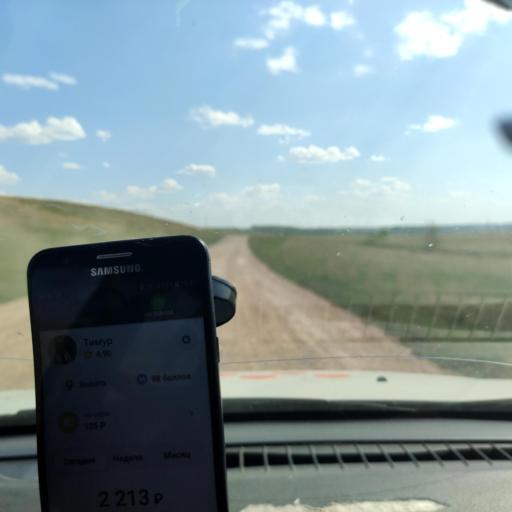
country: RU
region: Bashkortostan
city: Avdon
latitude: 54.5683
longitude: 55.6342
